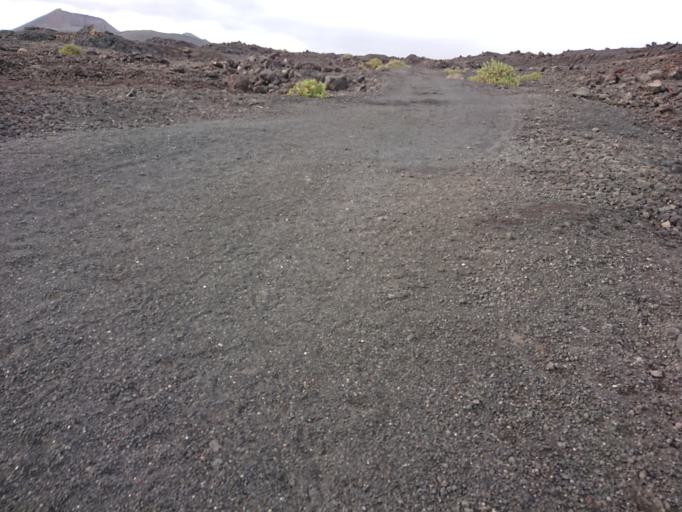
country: ES
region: Canary Islands
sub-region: Provincia de Las Palmas
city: Tias
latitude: 29.0011
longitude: -13.6910
